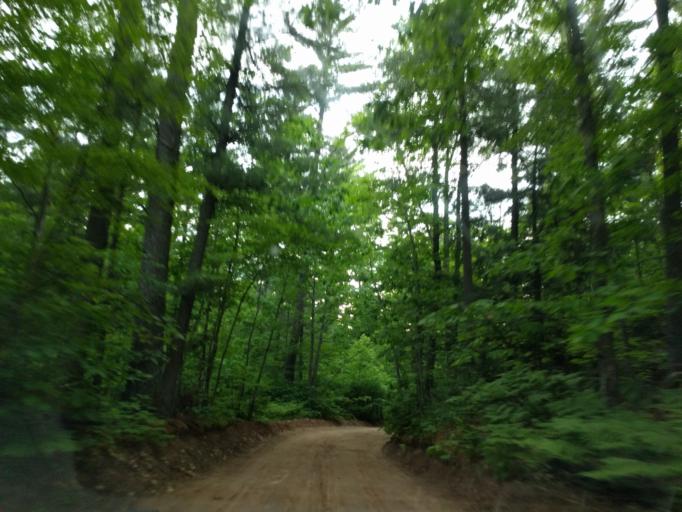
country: US
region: Michigan
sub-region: Marquette County
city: Trowbridge Park
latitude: 46.6047
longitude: -87.5024
